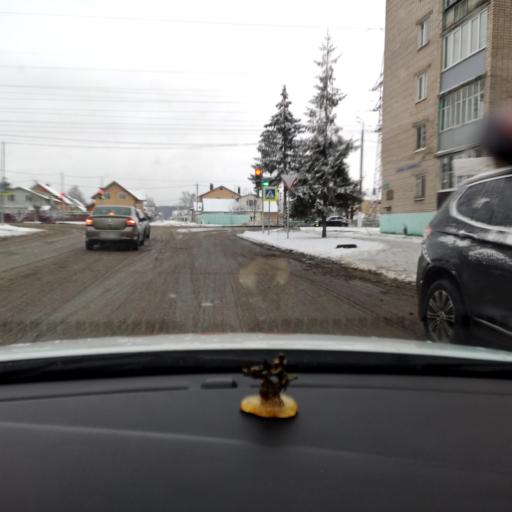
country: RU
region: Tatarstan
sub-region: Zelenodol'skiy Rayon
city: Zelenodolsk
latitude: 55.8512
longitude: 48.5253
